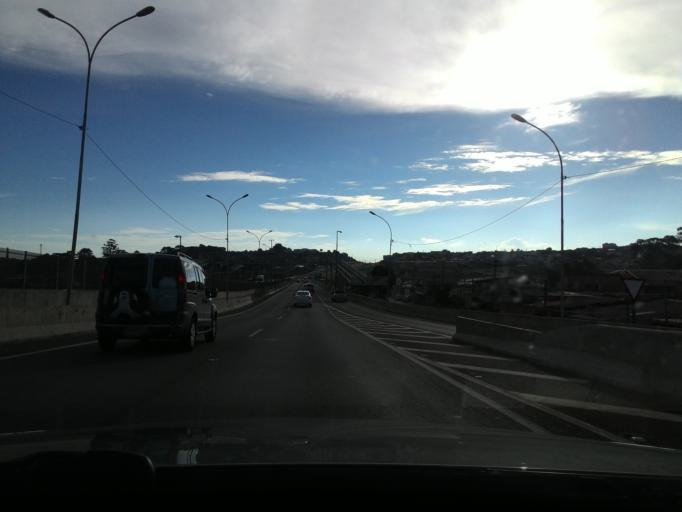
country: BR
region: Parana
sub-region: Pinhais
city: Pinhais
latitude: -25.3852
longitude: -49.1724
